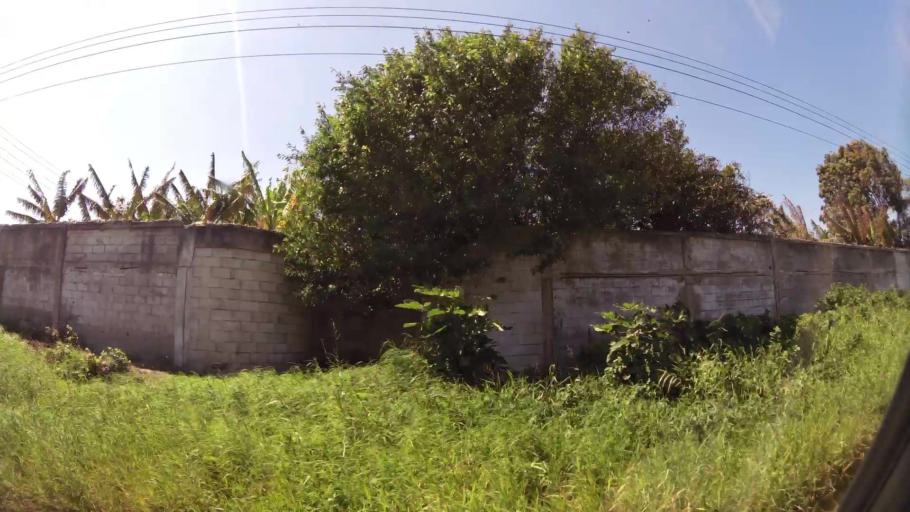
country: CO
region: Atlantico
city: Barranquilla
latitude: 10.9841
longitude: -74.7674
